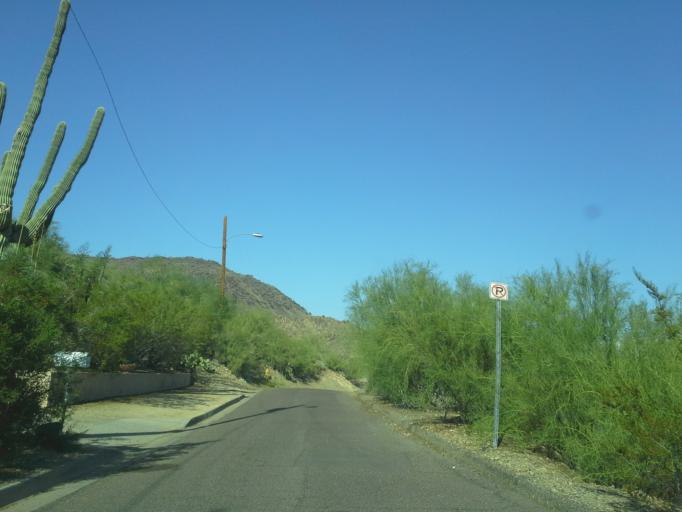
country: US
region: Arizona
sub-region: Maricopa County
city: Glendale
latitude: 33.5845
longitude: -112.0859
